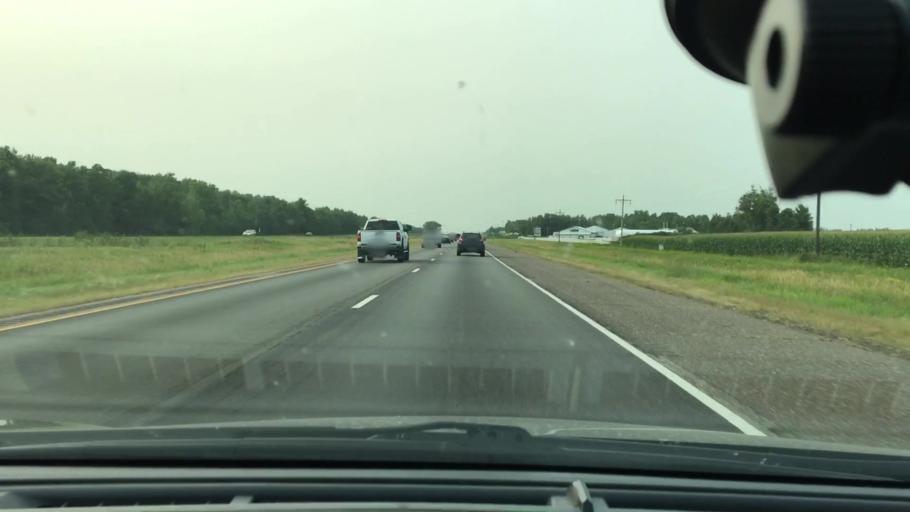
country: US
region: Minnesota
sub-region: Mille Lacs County
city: Princeton
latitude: 45.6336
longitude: -93.6169
